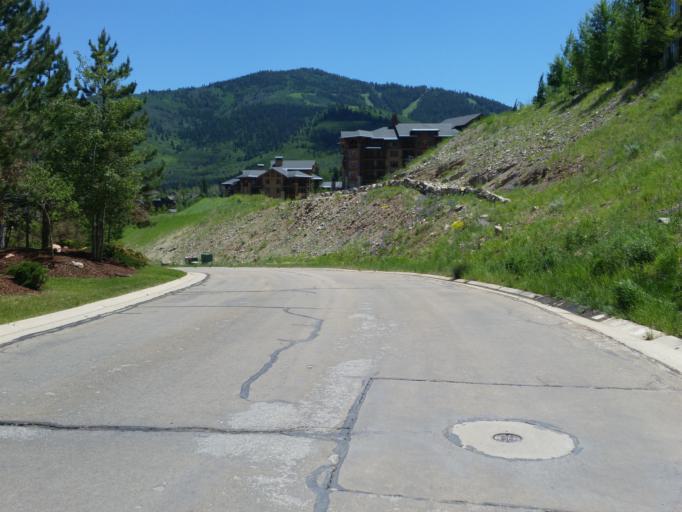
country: US
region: Utah
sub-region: Summit County
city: Snyderville
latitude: 40.6847
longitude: -111.5578
